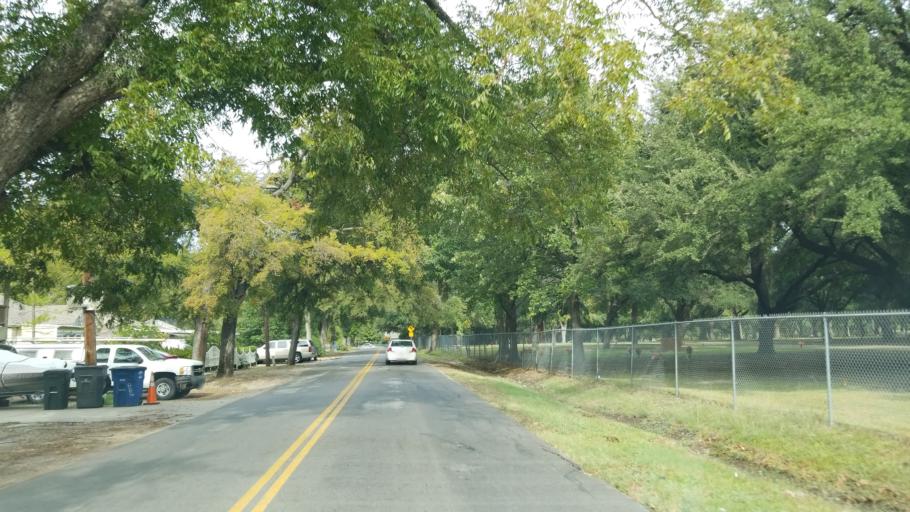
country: US
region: Texas
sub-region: Dallas County
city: Dallas
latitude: 32.7843
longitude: -96.7182
